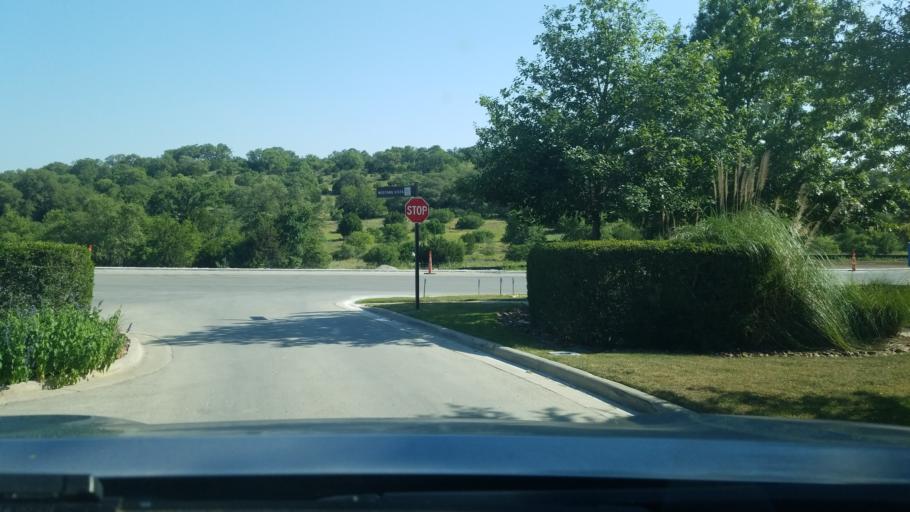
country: US
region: Texas
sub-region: Comal County
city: Bulverde
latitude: 29.7695
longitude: -98.4242
